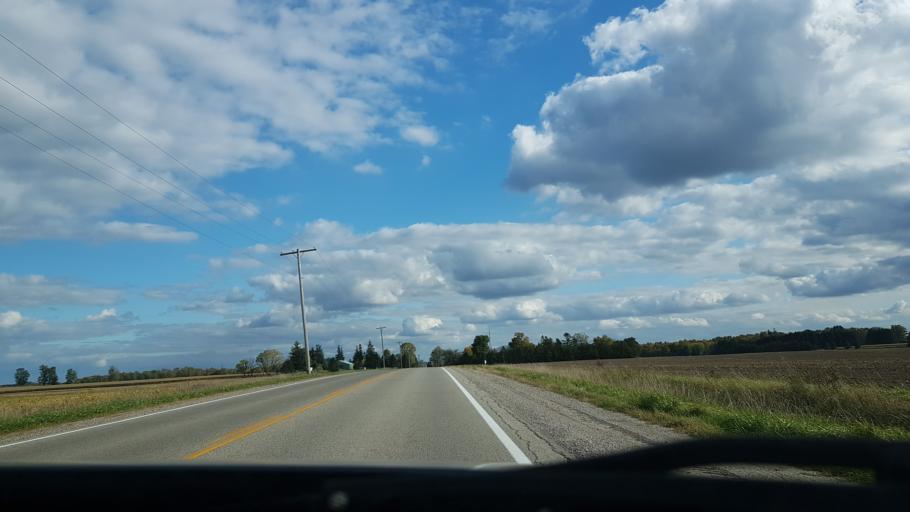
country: CA
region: Ontario
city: Delaware
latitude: 43.0163
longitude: -81.4436
